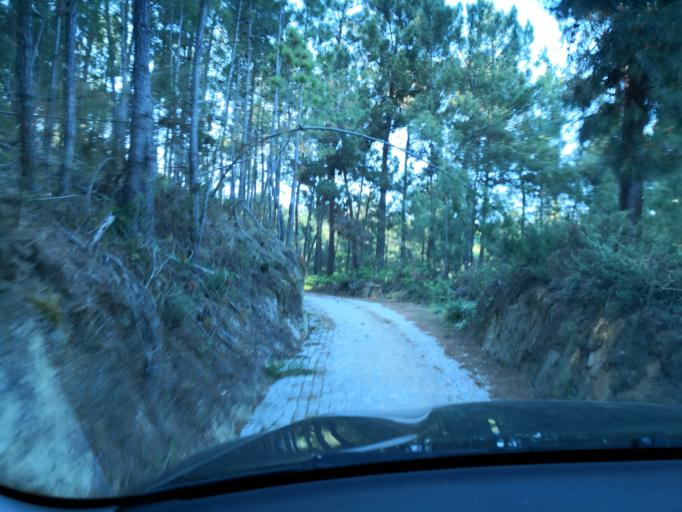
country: PT
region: Vila Real
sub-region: Vila Real
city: Vila Real
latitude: 41.3321
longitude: -7.7476
